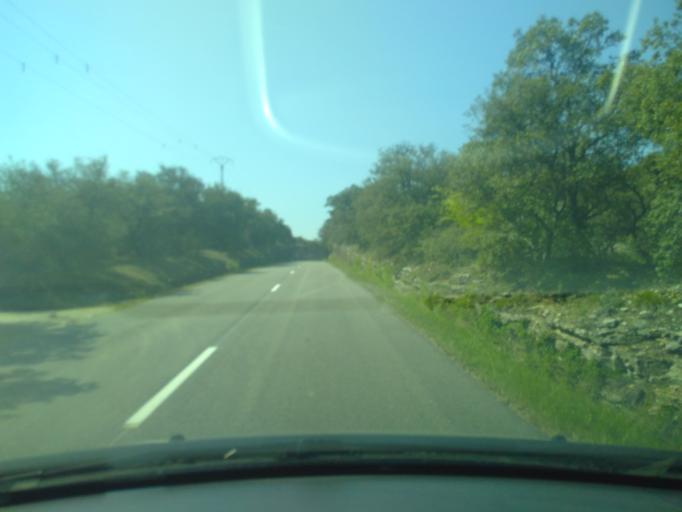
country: FR
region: Rhone-Alpes
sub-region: Departement de la Drome
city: Taulignan
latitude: 44.4462
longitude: 4.9572
